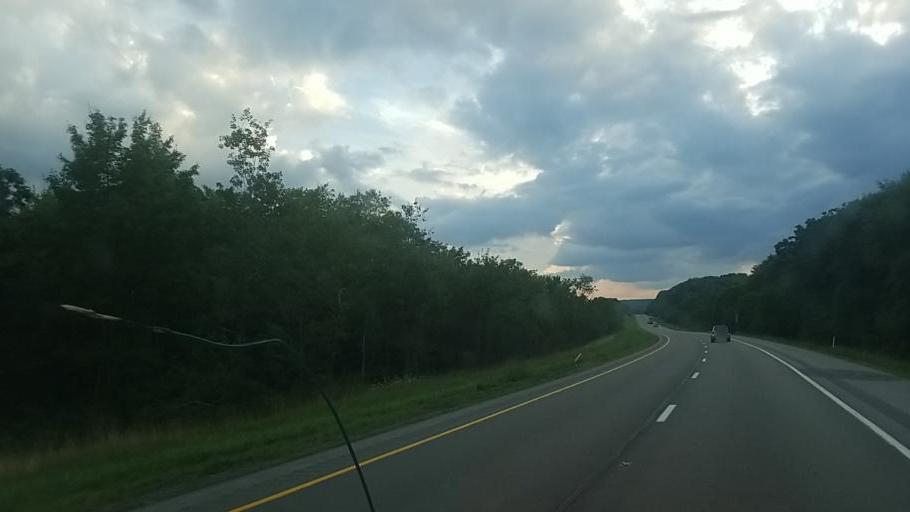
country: US
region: Pennsylvania
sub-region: Clearfield County
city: Treasure Lake
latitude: 41.1273
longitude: -78.5720
